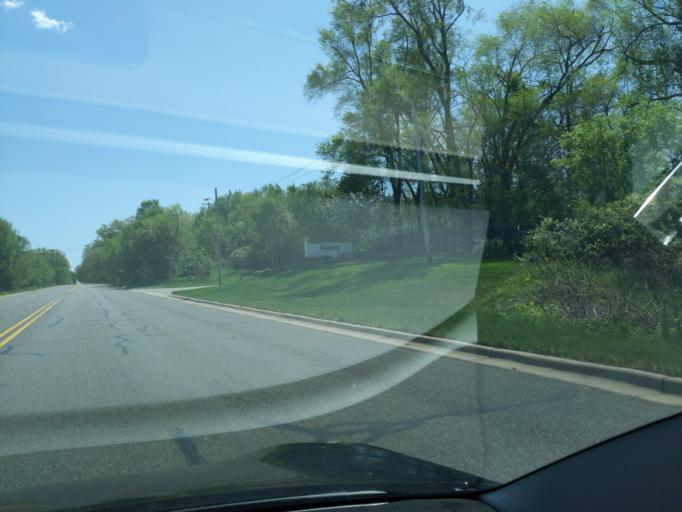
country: US
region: Michigan
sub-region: Kent County
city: Forest Hills
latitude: 42.9578
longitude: -85.5403
